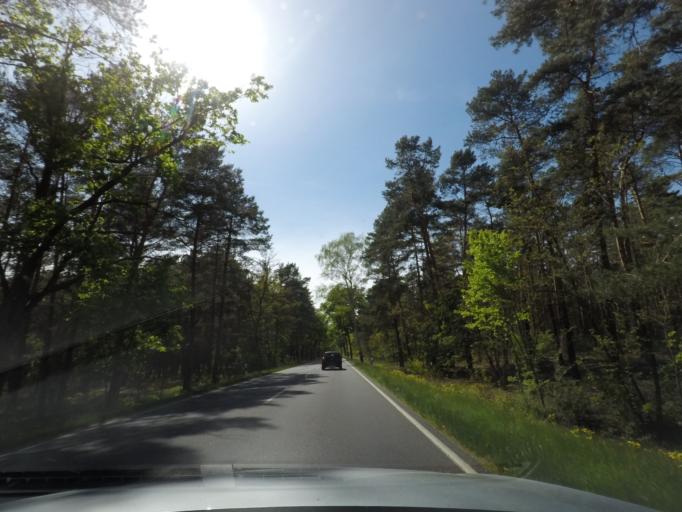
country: DE
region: Brandenburg
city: Luebben
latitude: 51.9458
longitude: 13.8333
